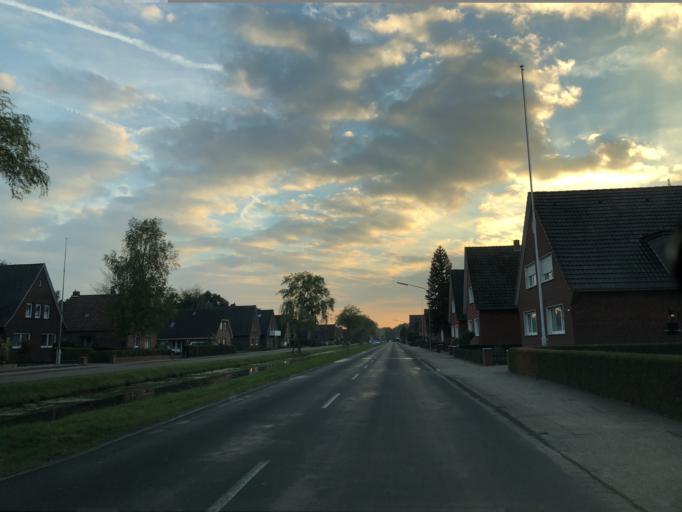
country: DE
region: Lower Saxony
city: Papenburg
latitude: 53.0690
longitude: 7.4429
